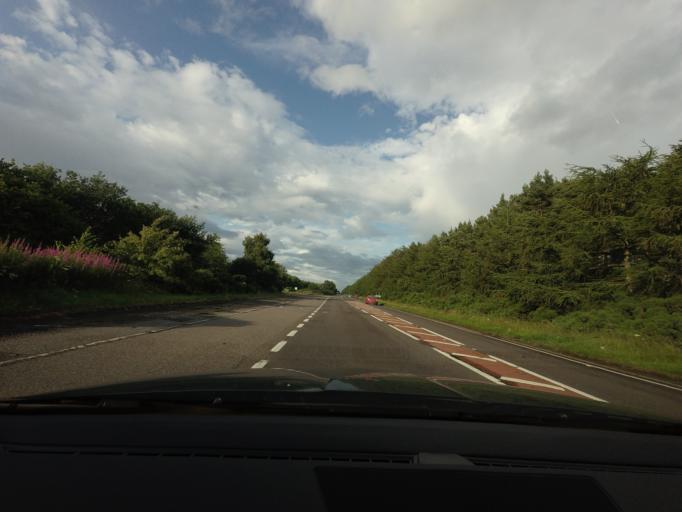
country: GB
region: Scotland
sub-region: Highland
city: Nairn
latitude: 57.5649
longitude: -3.9502
